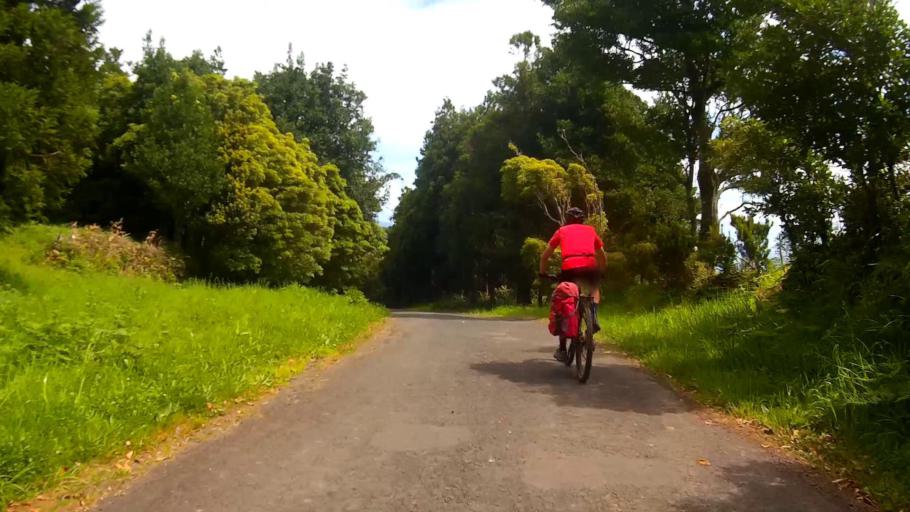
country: PT
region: Azores
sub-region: Horta
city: Horta
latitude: 38.5509
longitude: -28.6664
